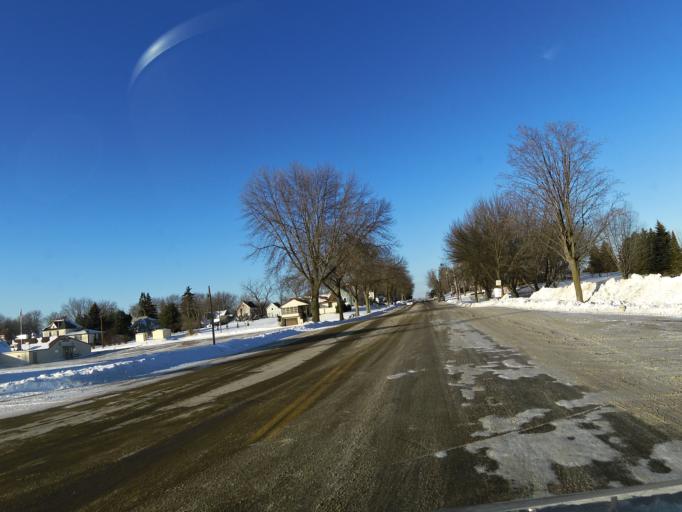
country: US
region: Minnesota
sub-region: Rice County
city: Lonsdale
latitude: 44.4816
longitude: -93.4286
